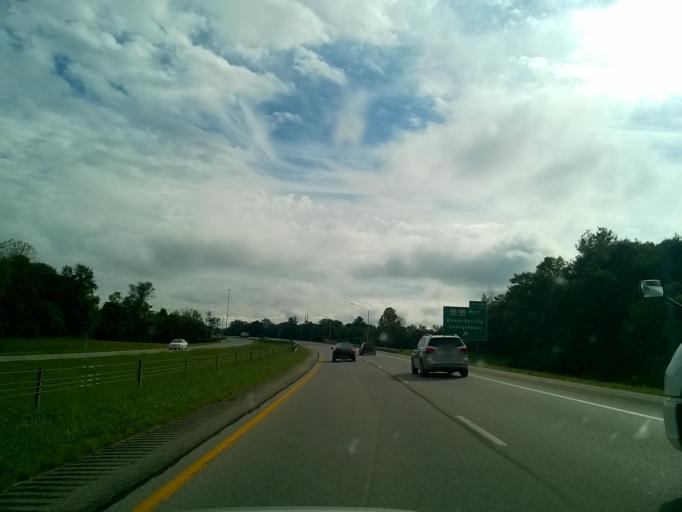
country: US
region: Indiana
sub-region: Floyd County
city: Georgetown
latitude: 38.2842
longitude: -85.9160
